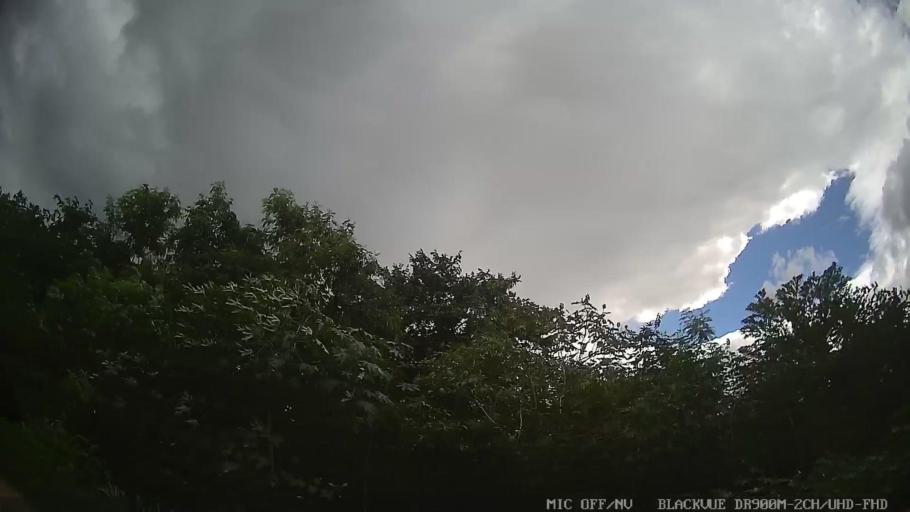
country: BR
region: Sao Paulo
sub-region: Jaguariuna
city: Jaguariuna
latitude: -22.6957
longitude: -46.9945
